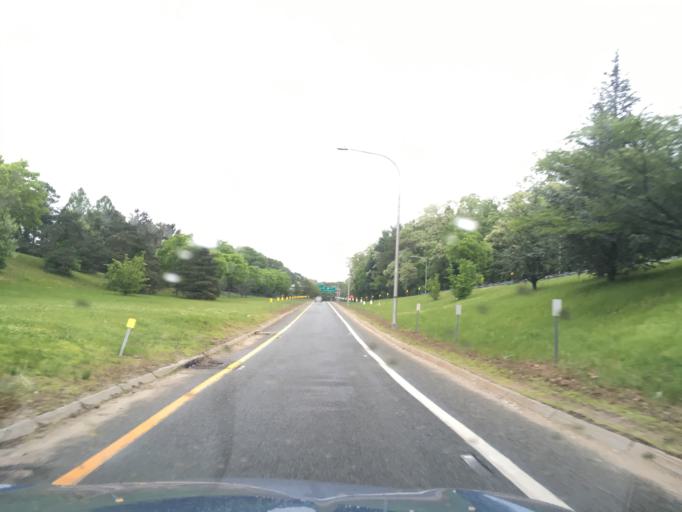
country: US
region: Rhode Island
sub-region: Providence County
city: Cranston
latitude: 41.7755
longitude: -71.4185
